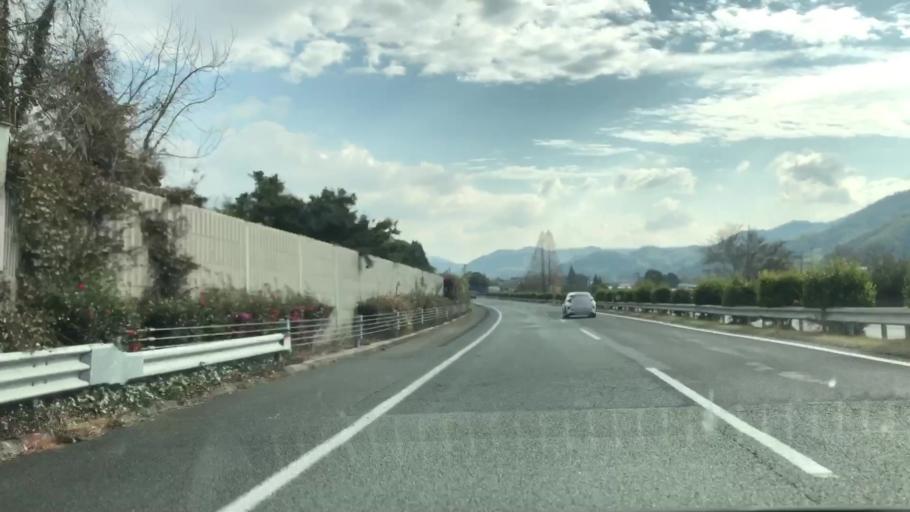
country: JP
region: Fukuoka
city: Setakamachi-takayanagi
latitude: 33.1243
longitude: 130.5189
